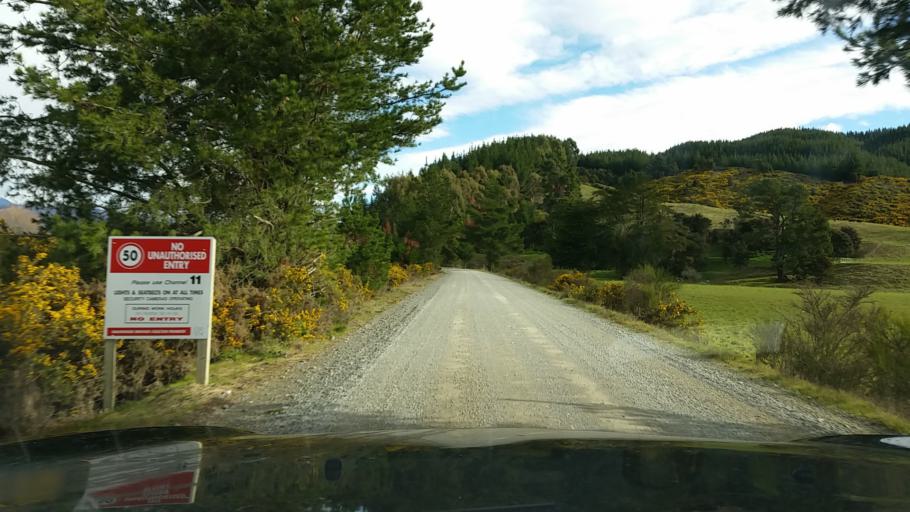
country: NZ
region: Nelson
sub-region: Nelson City
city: Nelson
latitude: -41.5708
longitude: 173.4499
